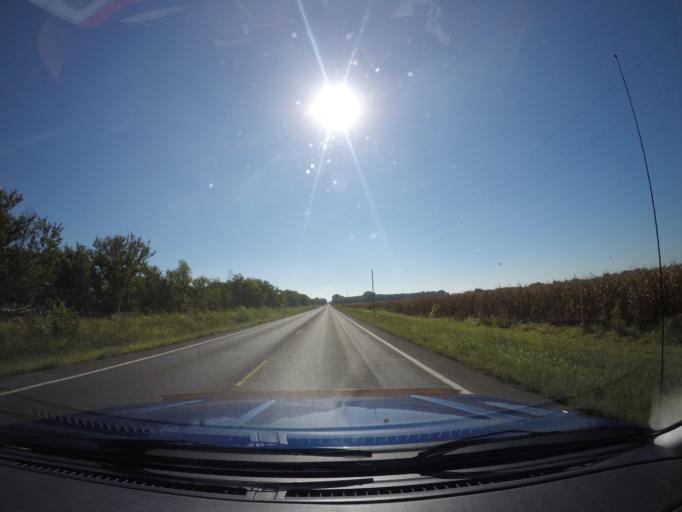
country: US
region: Kansas
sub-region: Pottawatomie County
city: Saint Marys
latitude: 39.2093
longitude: -96.1066
